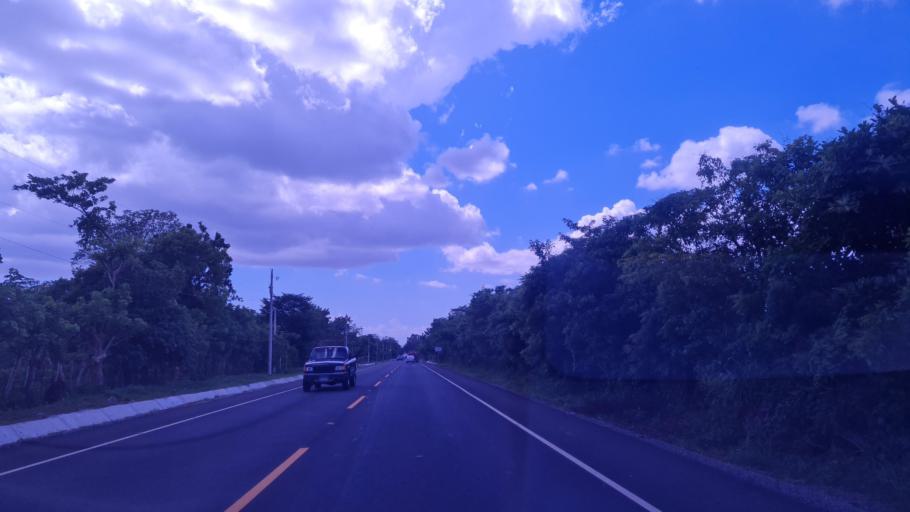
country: NI
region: Masaya
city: Nindiri
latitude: 12.0327
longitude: -86.1249
